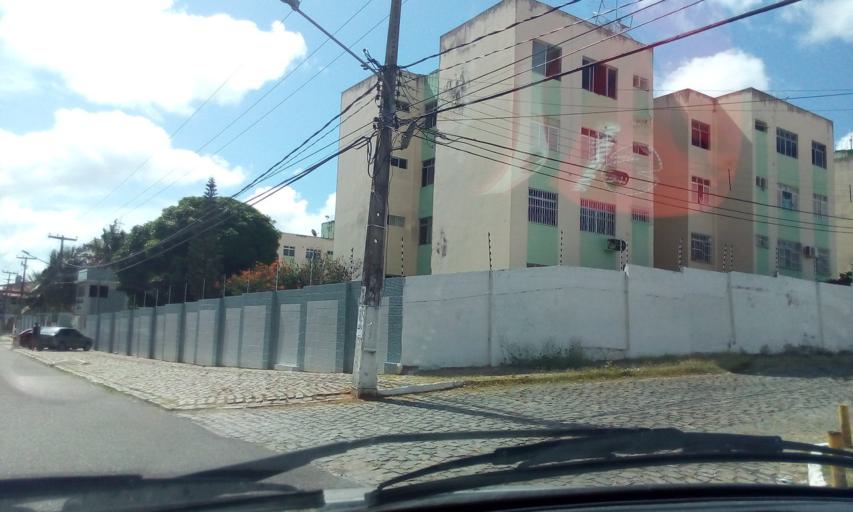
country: BR
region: Rio Grande do Norte
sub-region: Parnamirim
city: Parnamirim
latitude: -5.8797
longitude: -35.2073
